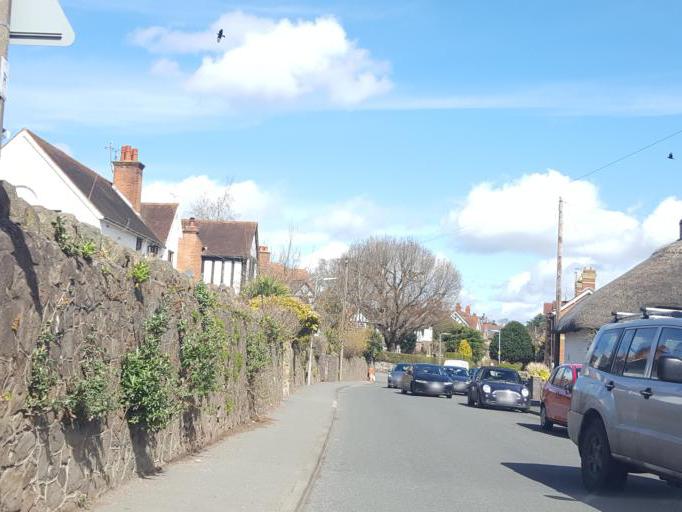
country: GB
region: England
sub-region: Worcestershire
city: Great Malvern
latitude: 52.1039
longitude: -2.3190
